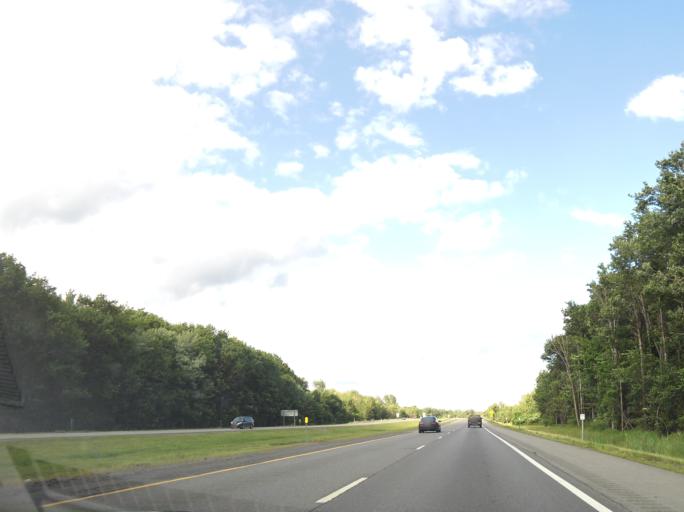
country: US
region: New York
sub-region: Erie County
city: Akron
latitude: 42.9907
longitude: -78.4408
